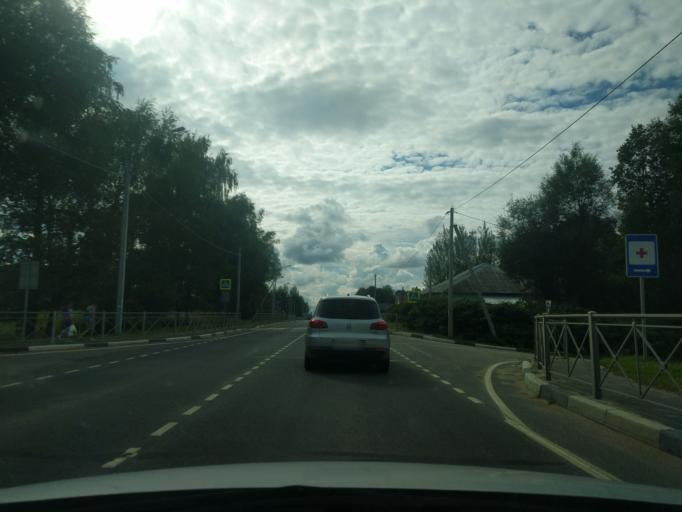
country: RU
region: Jaroslavl
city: Levashevo
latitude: 57.6442
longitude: 40.5327
